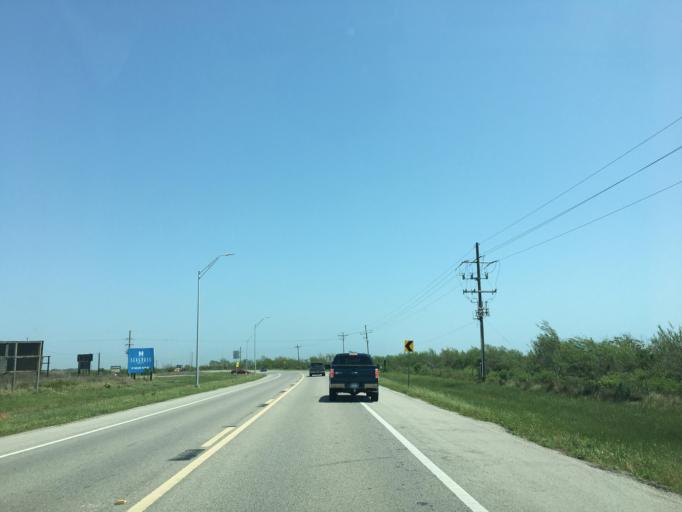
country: US
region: Texas
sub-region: Galveston County
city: Galveston
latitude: 29.3914
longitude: -94.7320
